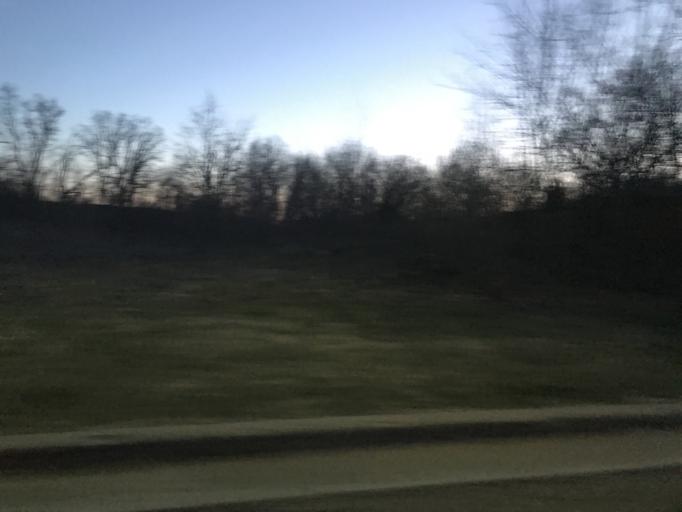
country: US
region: Michigan
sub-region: Livingston County
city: Brighton
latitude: 42.5477
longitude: -83.8000
